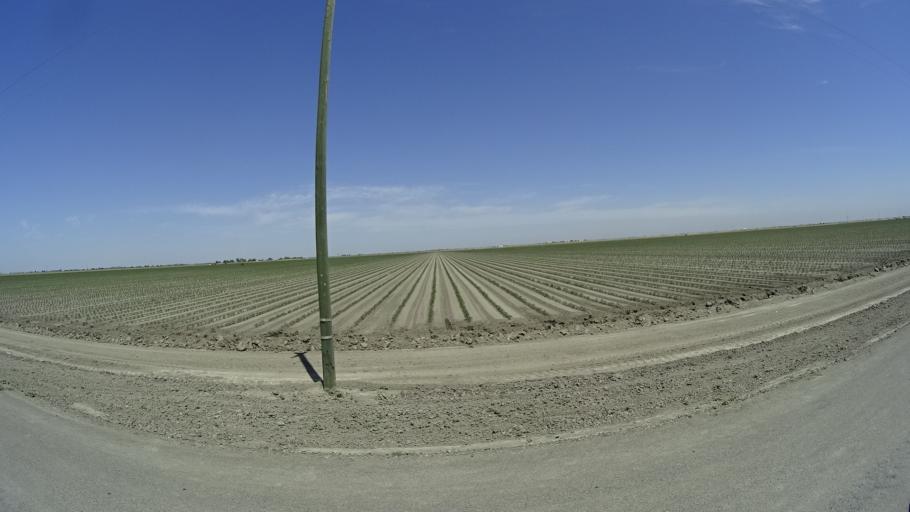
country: US
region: California
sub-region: Kings County
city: Stratford
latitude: 36.1234
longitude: -119.7098
